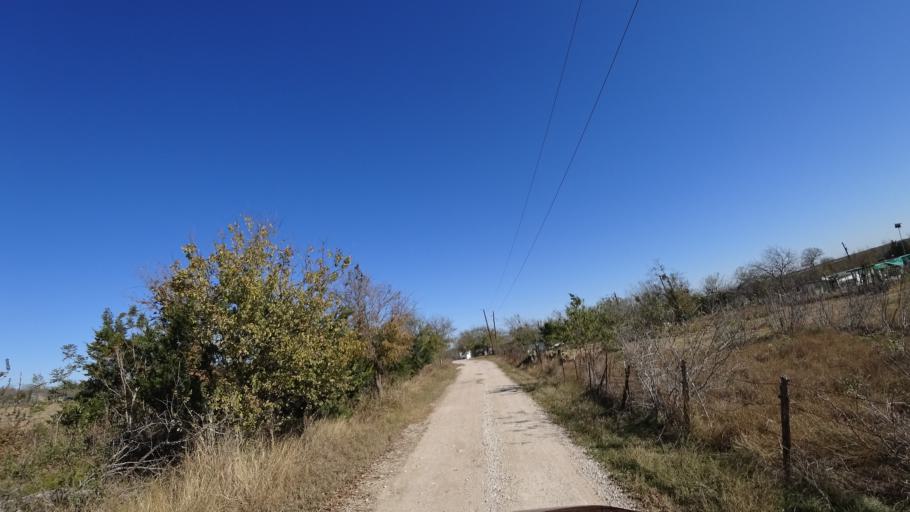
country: US
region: Texas
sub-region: Travis County
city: Garfield
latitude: 30.1198
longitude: -97.6278
